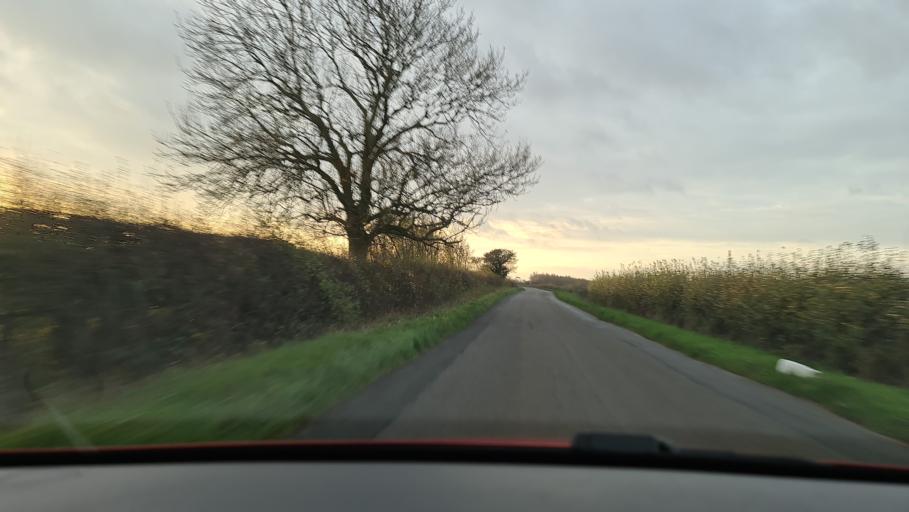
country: GB
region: England
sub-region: Oxfordshire
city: Somerton
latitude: 51.8962
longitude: -1.2749
